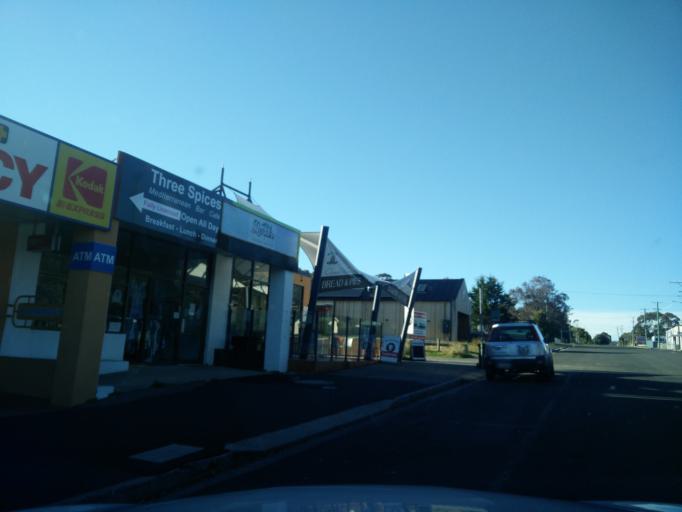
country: AU
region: Tasmania
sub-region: Break O'Day
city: St Helens
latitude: -41.8758
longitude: 148.3041
